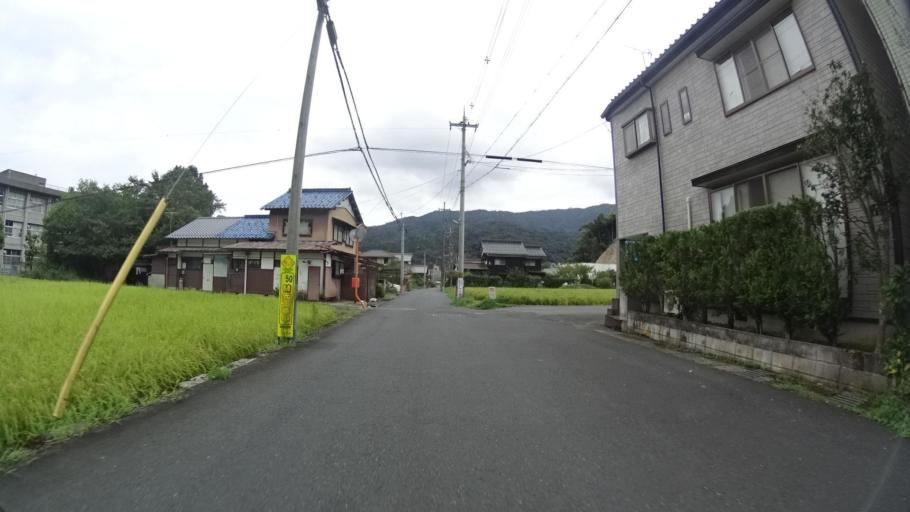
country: JP
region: Kyoto
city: Miyazu
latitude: 35.5287
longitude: 135.1878
